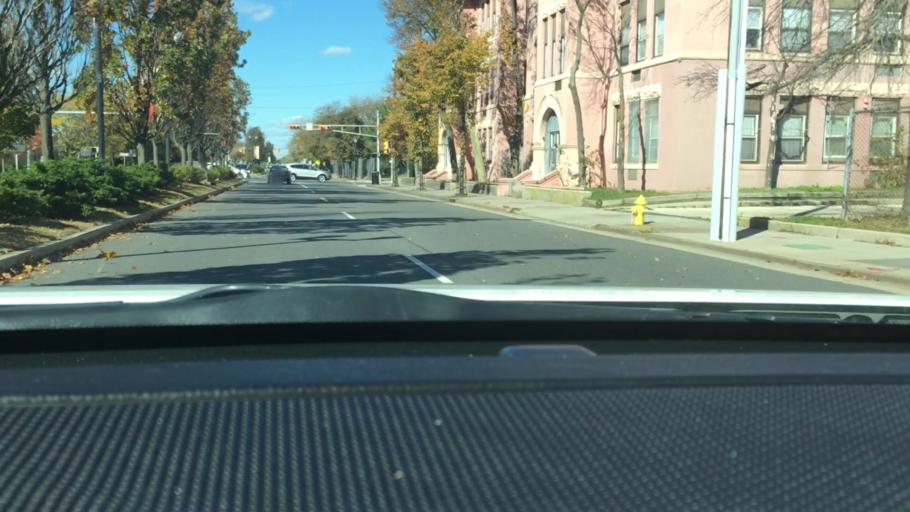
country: US
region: New Jersey
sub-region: Atlantic County
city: Atlantic City
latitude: 39.3615
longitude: -74.4324
